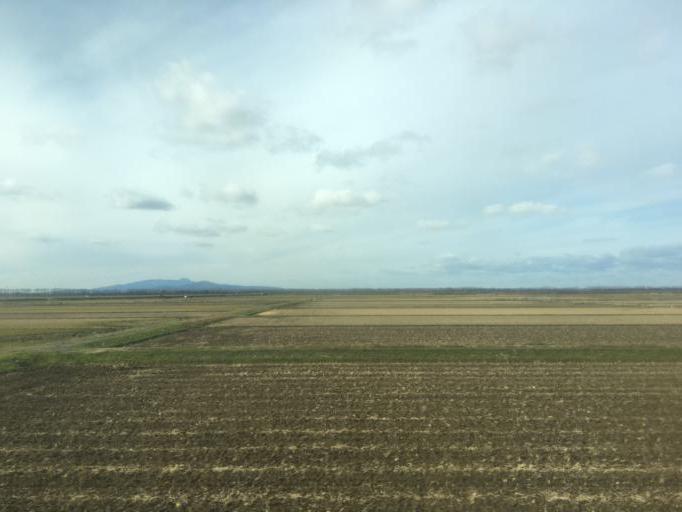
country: JP
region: Akita
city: Tenno
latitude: 39.9637
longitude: 140.0750
